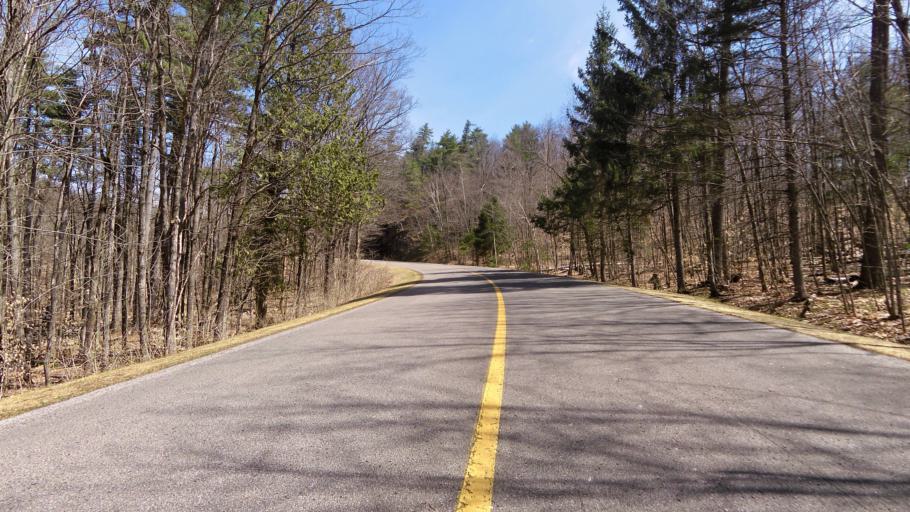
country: CA
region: Quebec
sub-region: Outaouais
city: Gatineau
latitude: 45.4891
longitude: -75.8558
